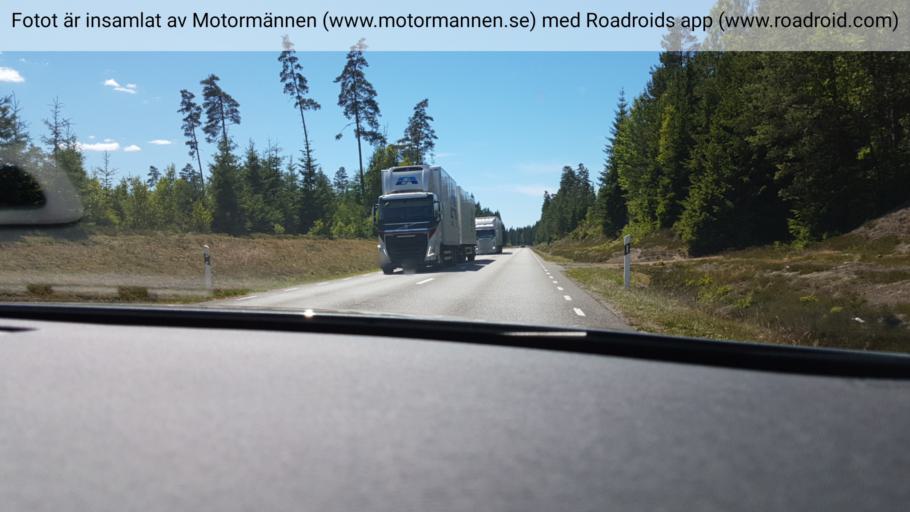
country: SE
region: Joenkoeping
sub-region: Gnosjo Kommun
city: Marieholm
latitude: 57.6349
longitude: 13.7888
